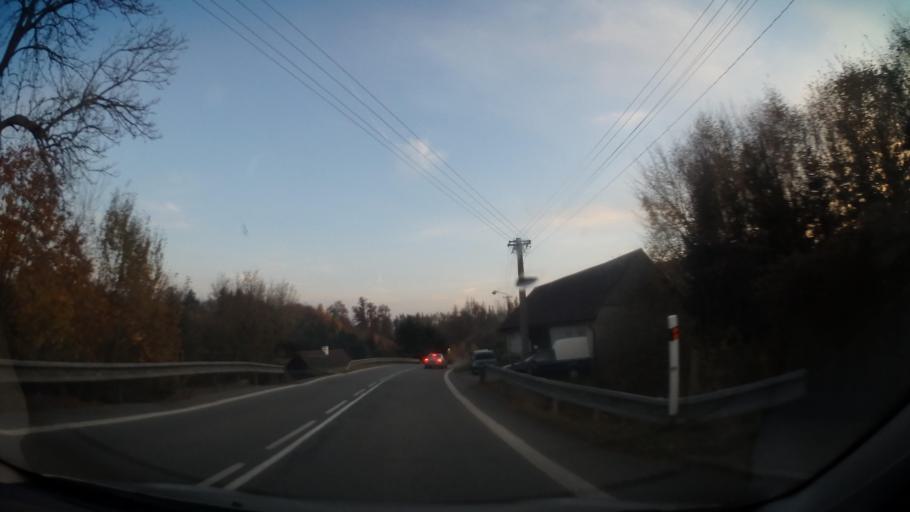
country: CZ
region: Vysocina
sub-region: Okres Pelhrimov
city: Zeliv
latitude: 49.5346
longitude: 15.1678
